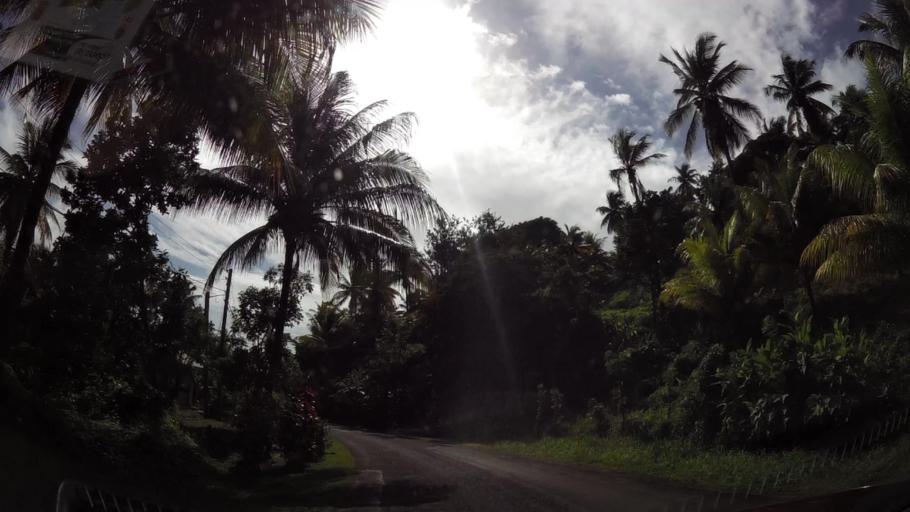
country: DM
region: Saint David
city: Castle Bruce
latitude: 15.4688
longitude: -61.2491
